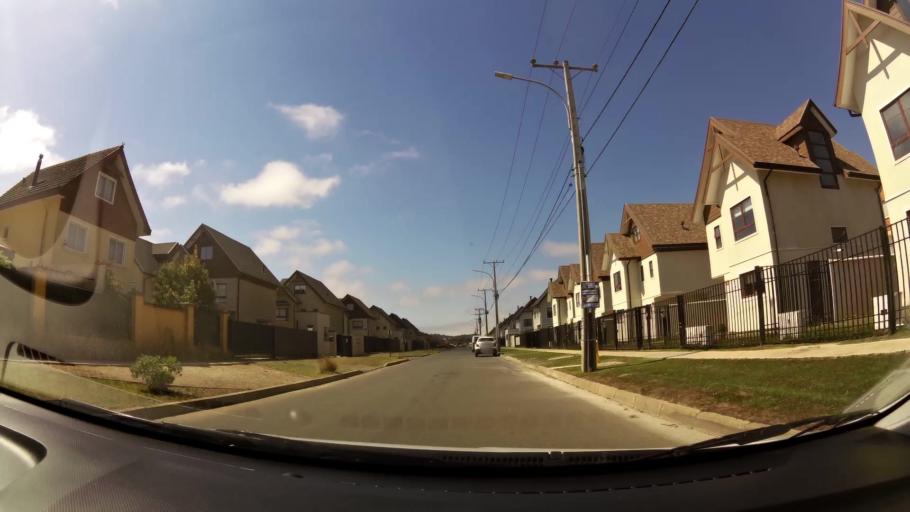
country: CL
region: Biobio
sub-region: Provincia de Concepcion
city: Concepcion
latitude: -36.7798
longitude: -73.0478
